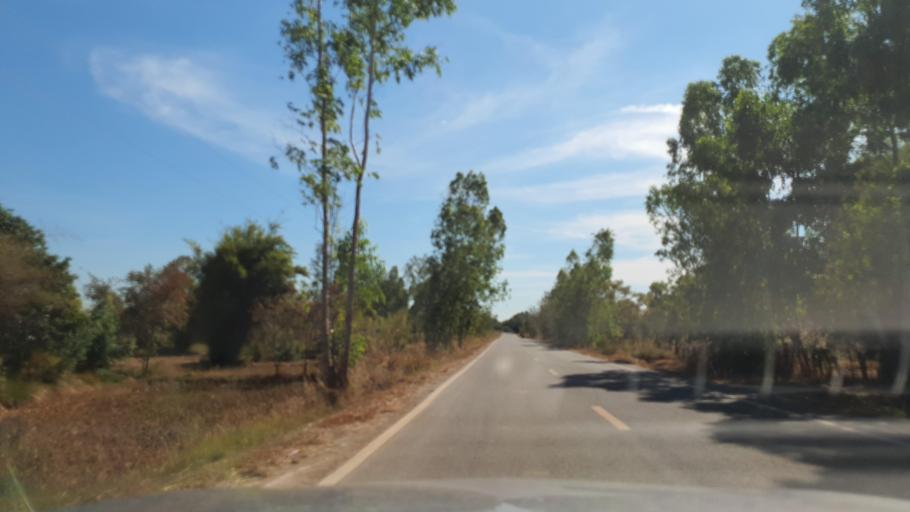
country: TH
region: Kalasin
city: Khao Wong
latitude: 16.6997
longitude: 104.1131
